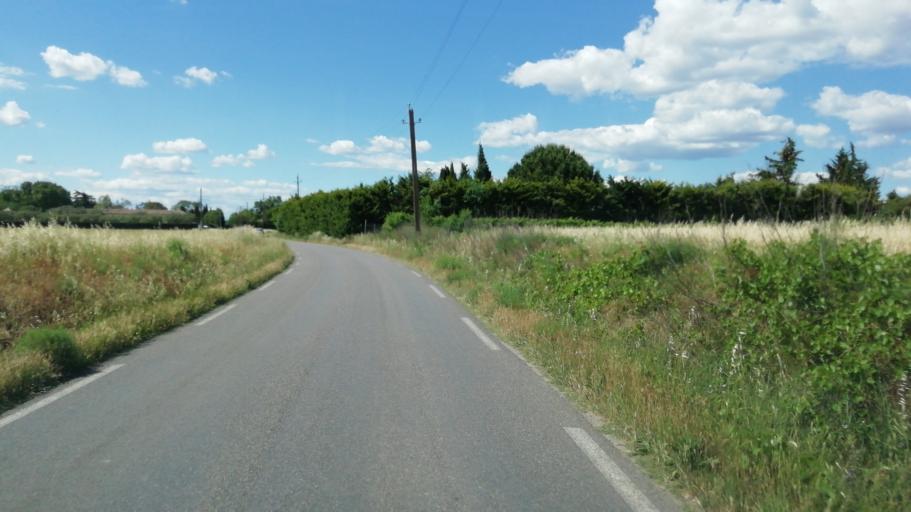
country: FR
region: Languedoc-Roussillon
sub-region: Departement de l'Herault
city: Saint-Just
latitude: 43.6662
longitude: 4.1058
